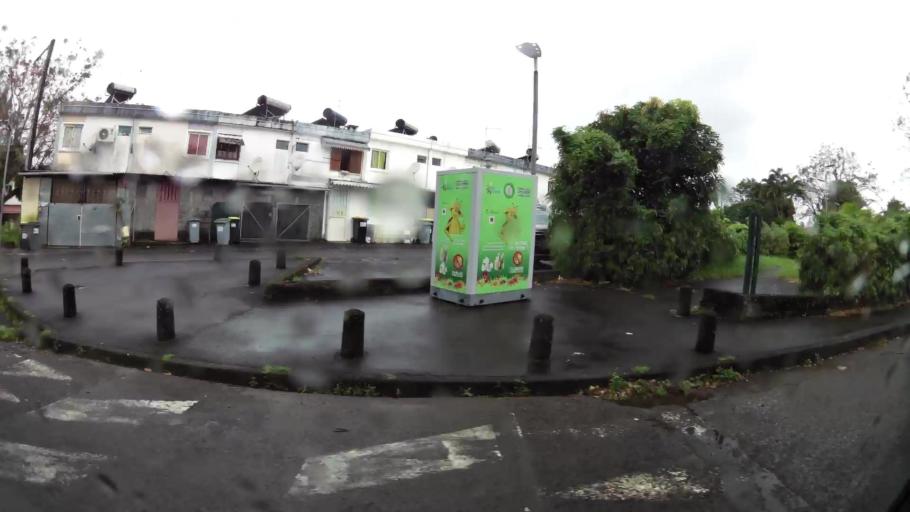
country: RE
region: Reunion
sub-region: Reunion
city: Saint-Andre
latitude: -20.9584
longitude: 55.6465
